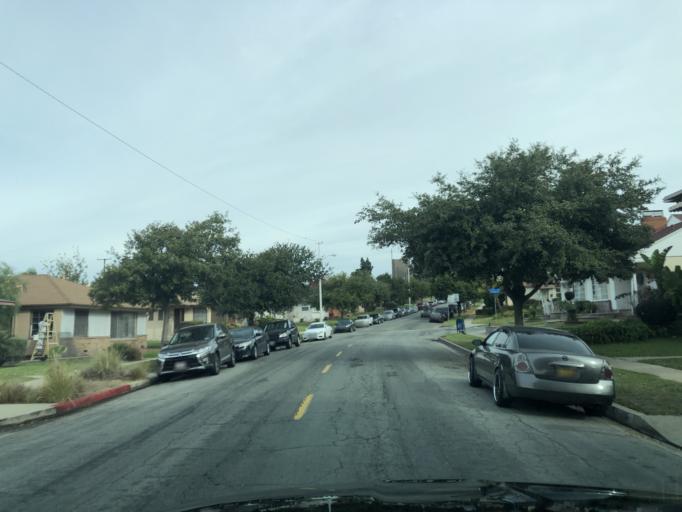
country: US
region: California
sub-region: Los Angeles County
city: Ladera Heights
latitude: 33.9838
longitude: -118.3663
